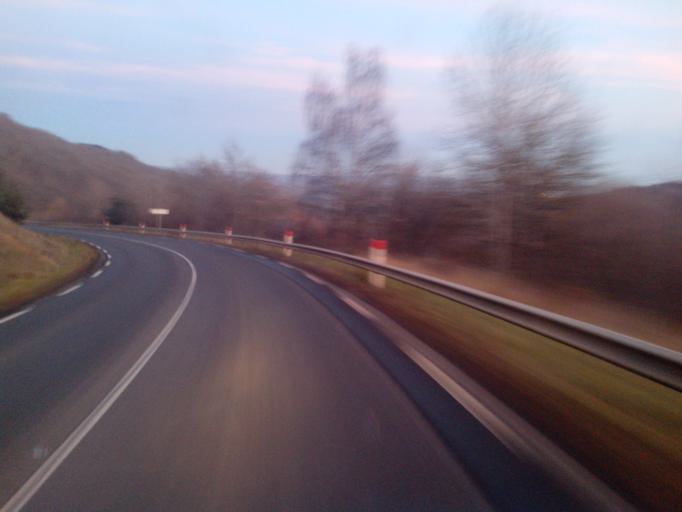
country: FR
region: Auvergne
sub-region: Departement du Cantal
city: Saint-Flour
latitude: 45.0526
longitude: 3.0153
